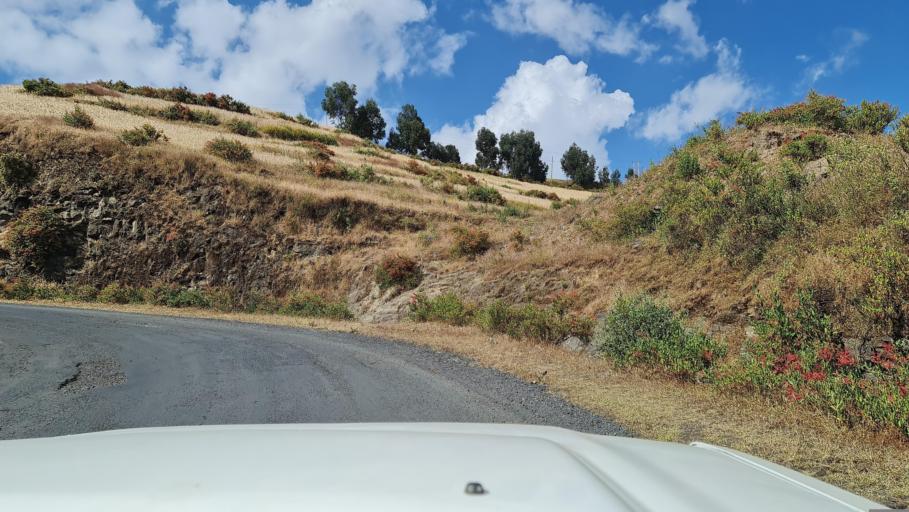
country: ET
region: Amhara
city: Debark'
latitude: 13.1372
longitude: 37.9368
